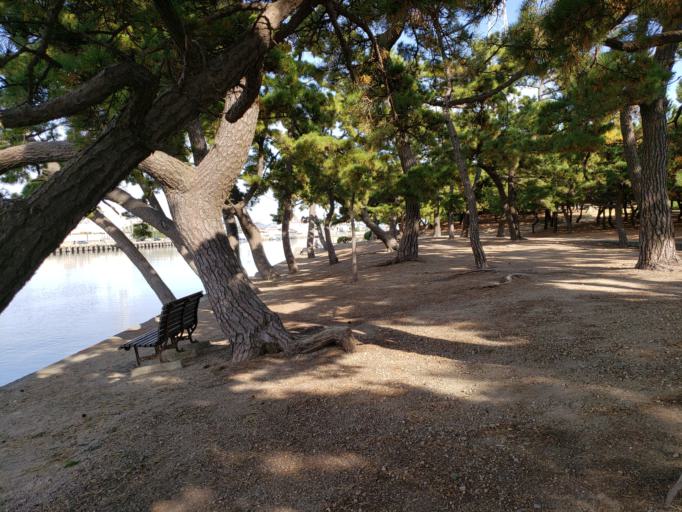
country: JP
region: Hyogo
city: Kakogawacho-honmachi
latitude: 34.7338
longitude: 134.8018
